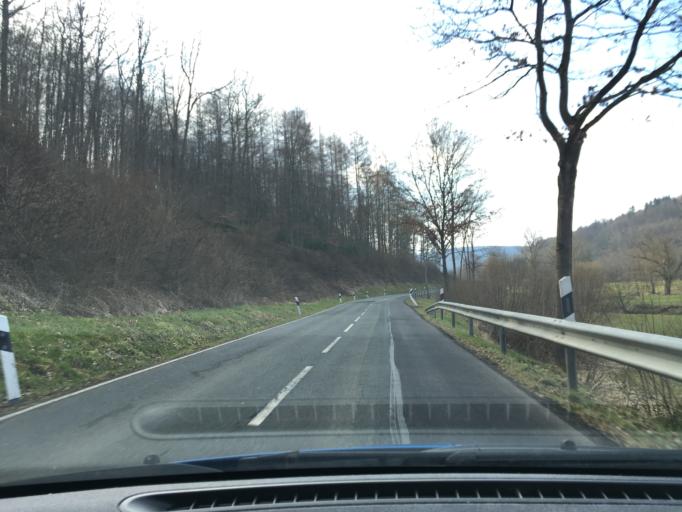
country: DE
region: Lower Saxony
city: Uslar
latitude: 51.6196
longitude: 9.6489
